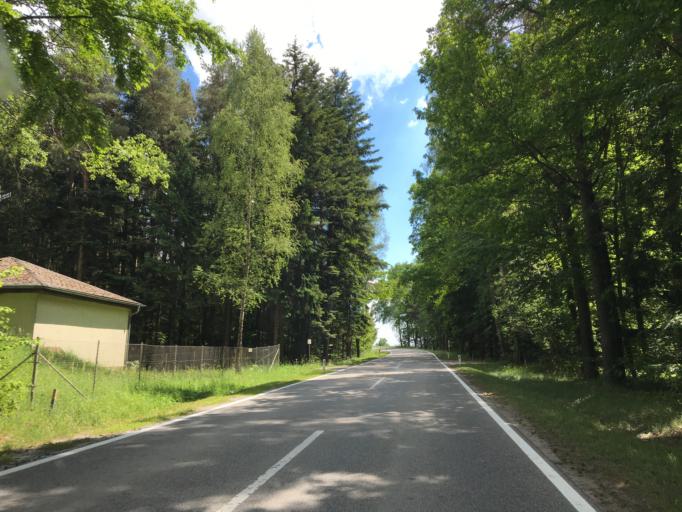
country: AT
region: Upper Austria
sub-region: Politischer Bezirk Freistadt
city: Freistadt
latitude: 48.4543
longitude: 14.5045
